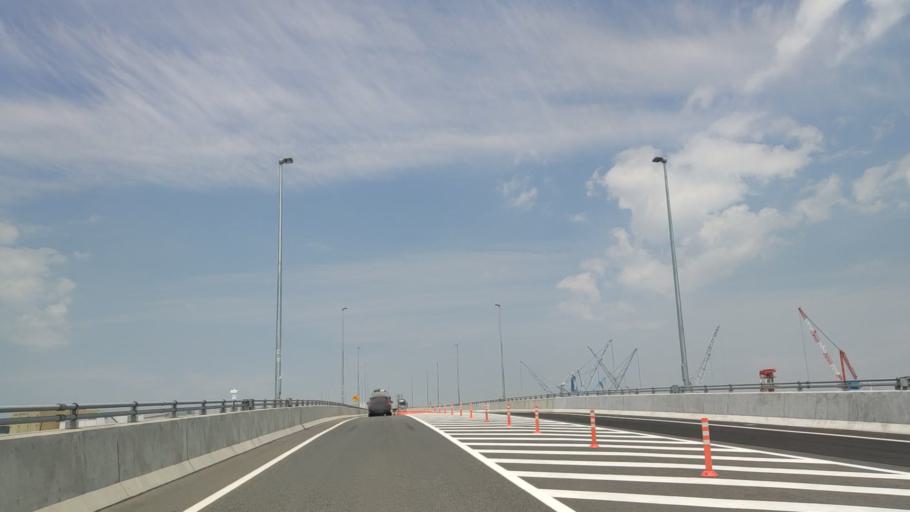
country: JP
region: Kanagawa
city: Yokohama
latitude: 35.4100
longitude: 139.6830
